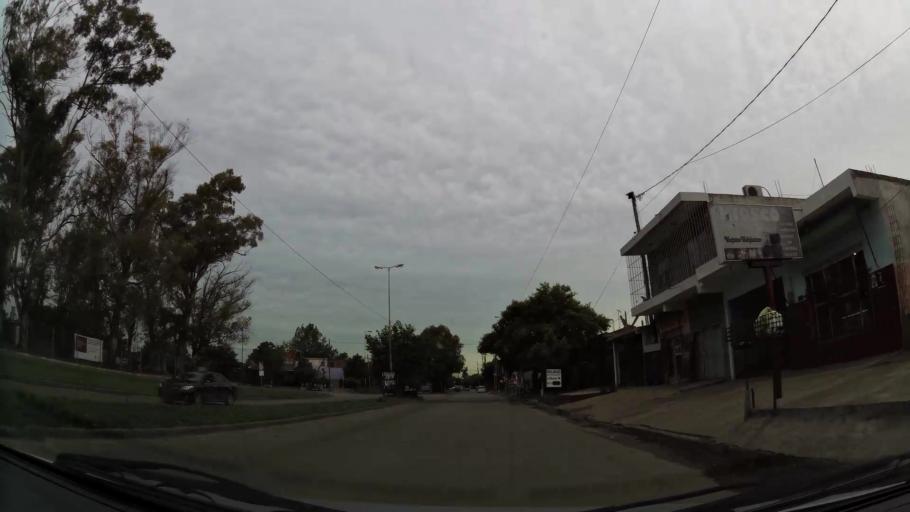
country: AR
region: Buenos Aires
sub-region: Partido de Lanus
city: Lanus
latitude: -34.7256
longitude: -58.3475
